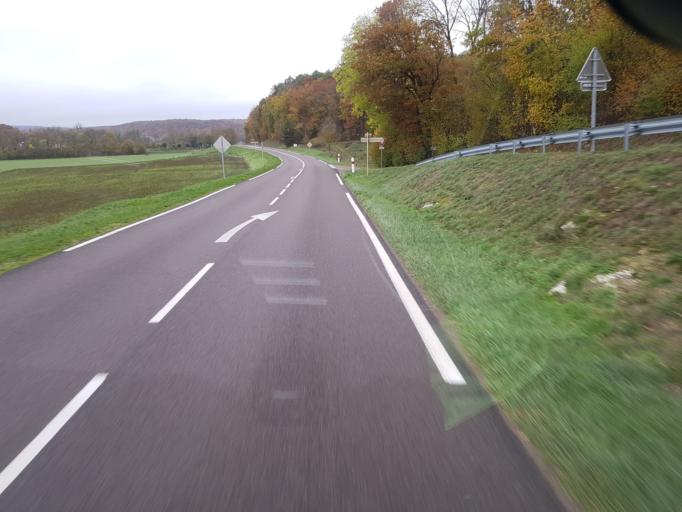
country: FR
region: Bourgogne
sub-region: Departement de la Cote-d'Or
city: Is-sur-Tille
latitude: 47.5307
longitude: 4.9929
